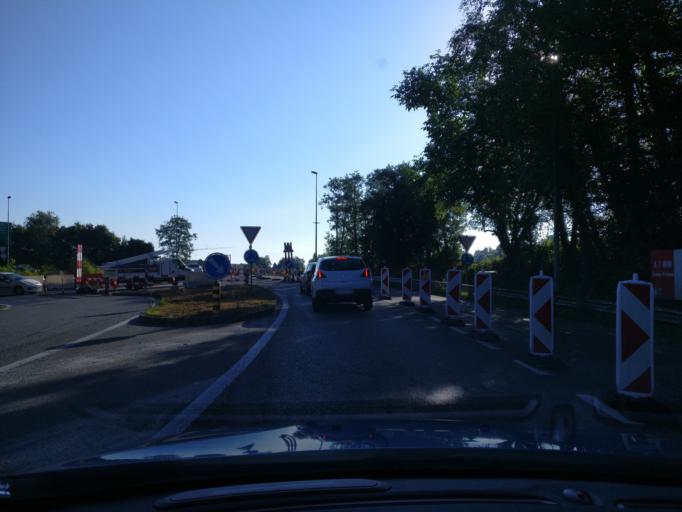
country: CH
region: Geneva
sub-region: Geneva
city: Le Grand-Saconnex
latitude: 46.2413
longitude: 6.1250
